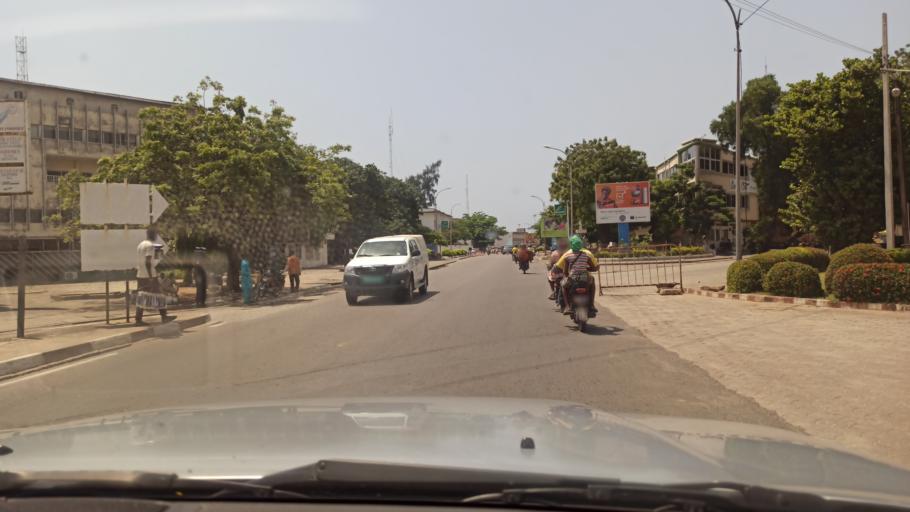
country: BJ
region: Littoral
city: Cotonou
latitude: 6.3537
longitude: 2.4353
